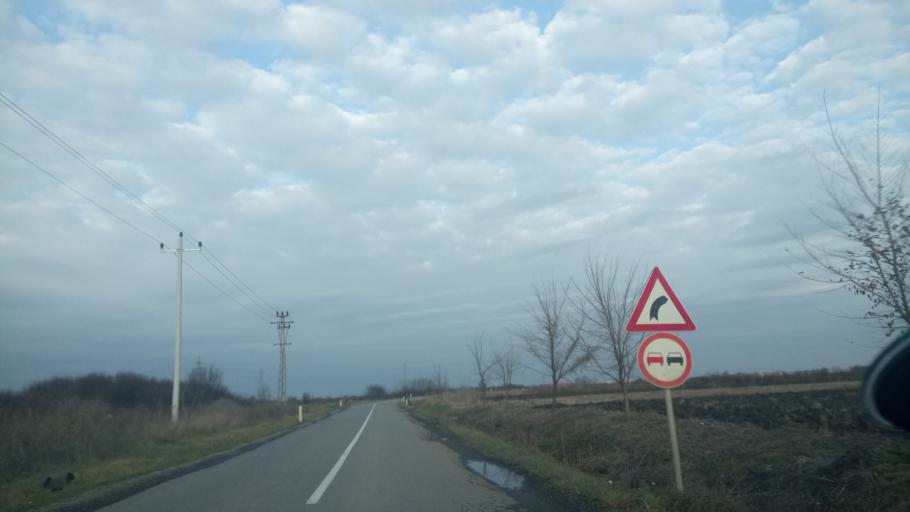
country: RS
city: Vojka
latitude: 44.9448
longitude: 20.1738
